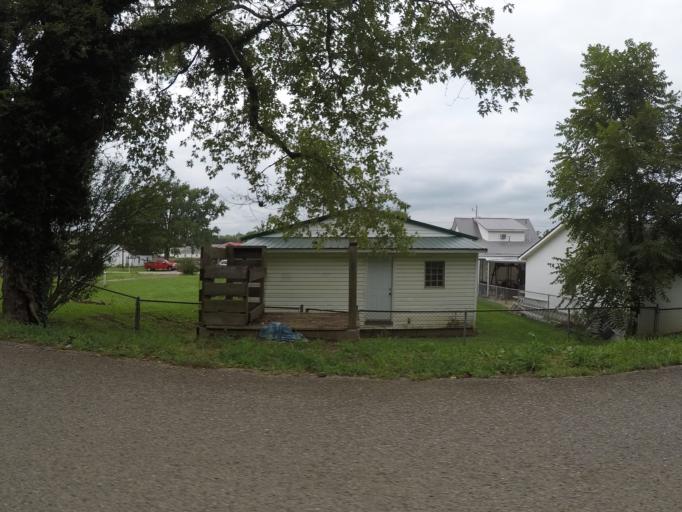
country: US
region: West Virginia
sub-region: Cabell County
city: Pea Ridge
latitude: 38.4273
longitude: -82.3781
